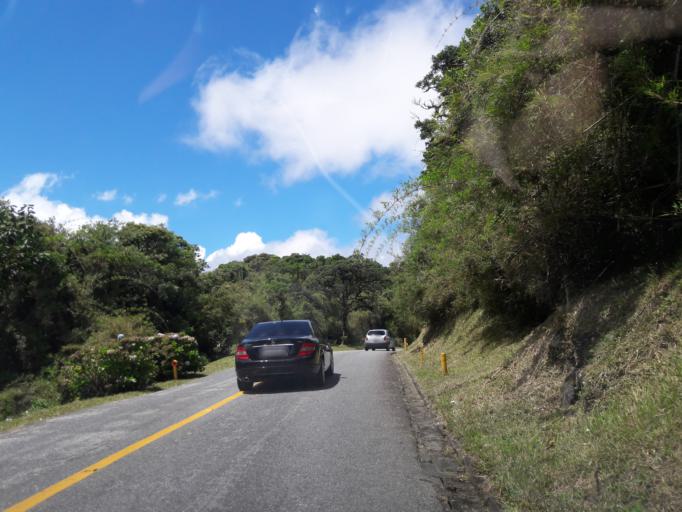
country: BR
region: Parana
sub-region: Campina Grande Do Sul
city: Campina Grande do Sul
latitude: -25.3322
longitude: -48.9027
